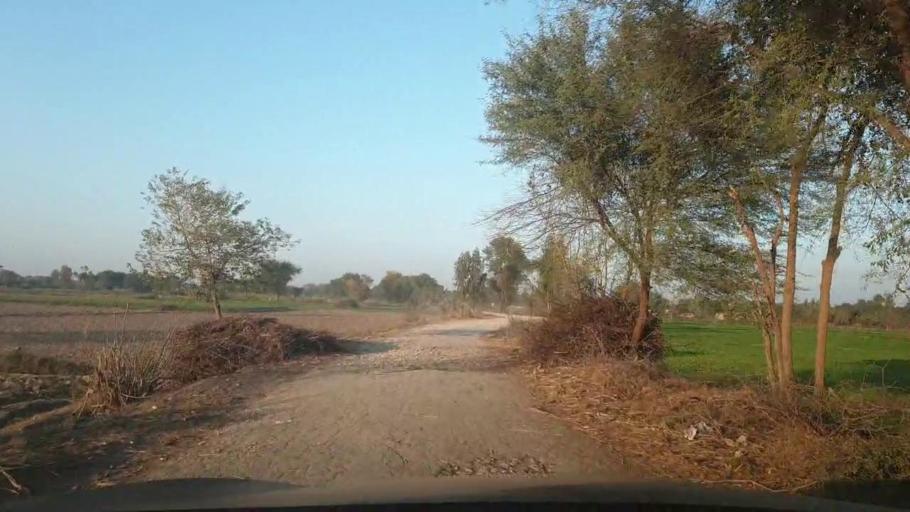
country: PK
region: Sindh
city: Ubauro
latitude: 28.1741
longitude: 69.6027
